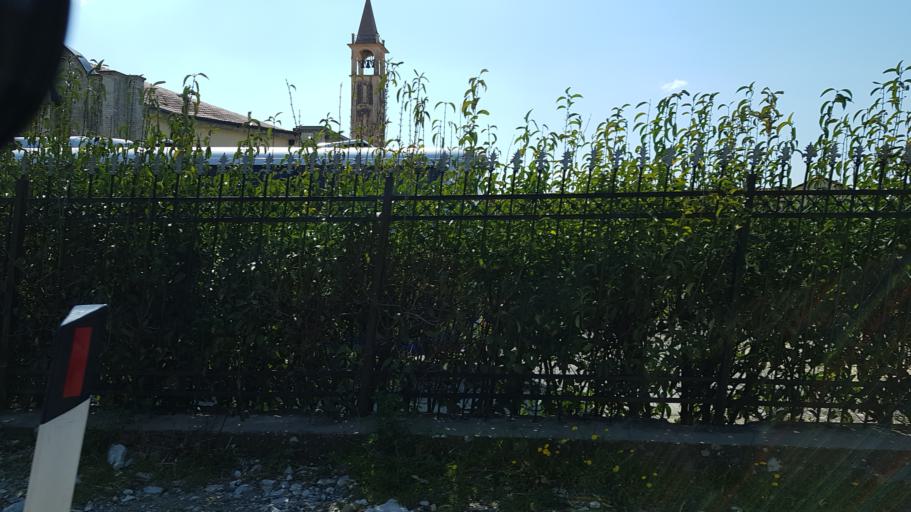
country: AL
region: Shkoder
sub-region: Rrethi i Shkodres
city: Guri i Zi
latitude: 42.0240
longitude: 19.5753
